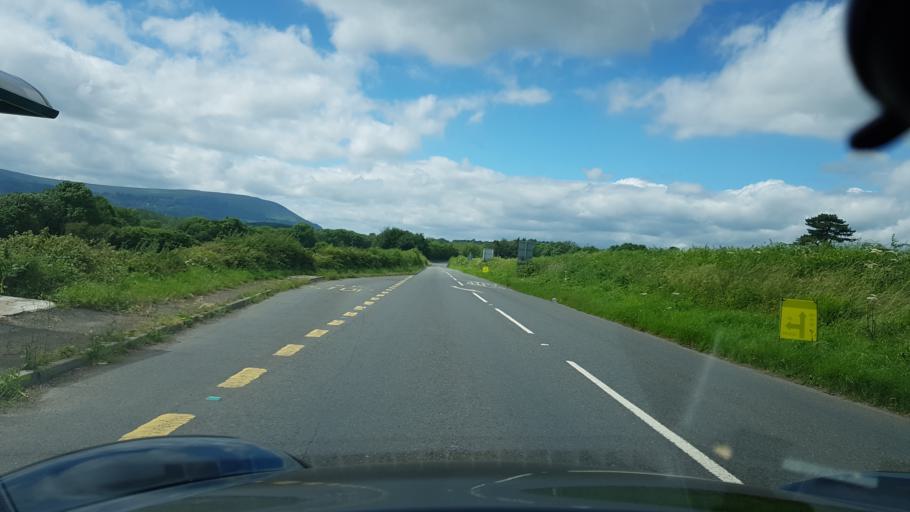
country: GB
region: Wales
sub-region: Monmouthshire
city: Llanarth
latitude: 51.7815
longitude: -2.9480
